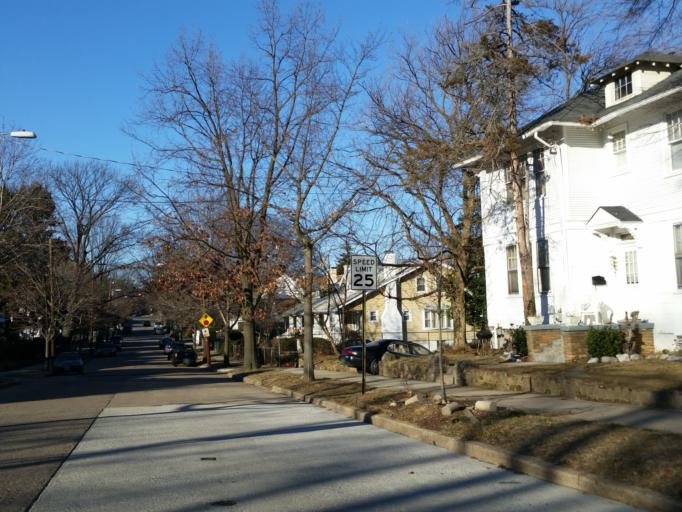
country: US
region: Maryland
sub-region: Montgomery County
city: Takoma Park
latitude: 38.9687
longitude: -77.0242
